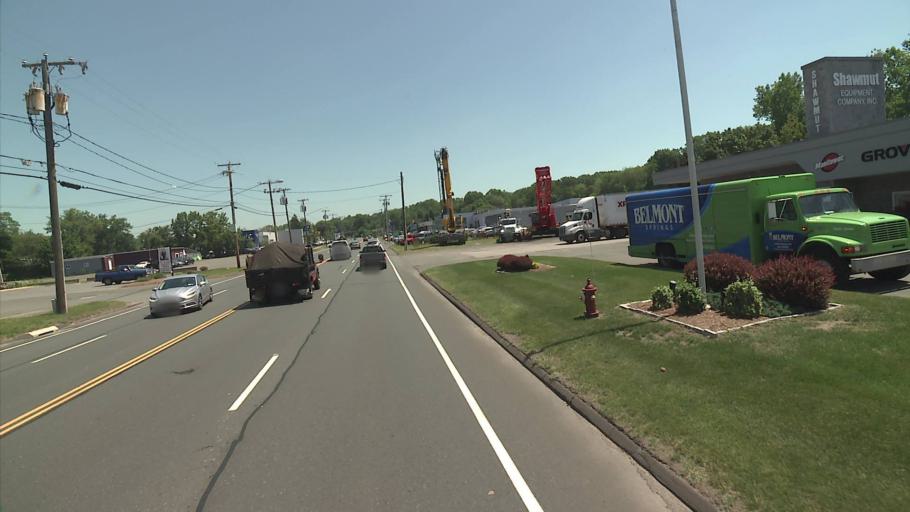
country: US
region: Connecticut
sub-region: Hartford County
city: Manchester
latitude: 41.8150
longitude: -72.5073
